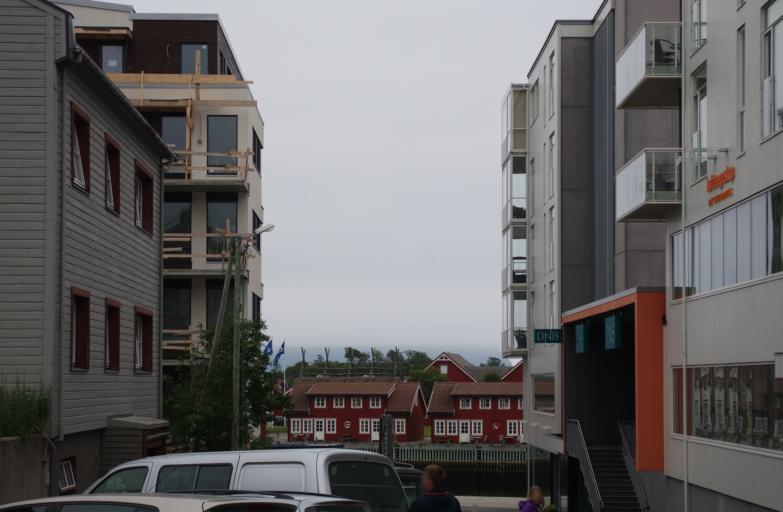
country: NO
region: Nordland
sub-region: Vagan
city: Svolvaer
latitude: 68.2343
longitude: 14.5667
